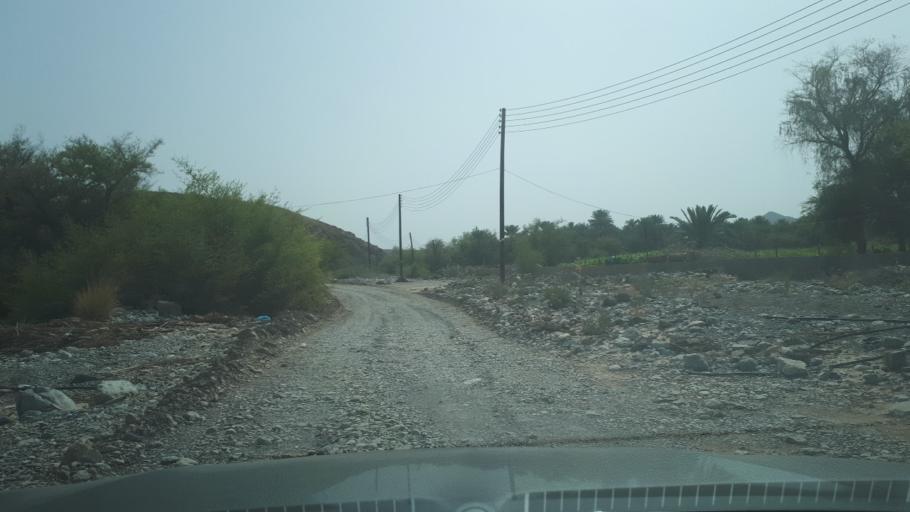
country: OM
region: Muhafazat ad Dakhiliyah
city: Bahla'
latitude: 23.2278
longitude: 57.0647
